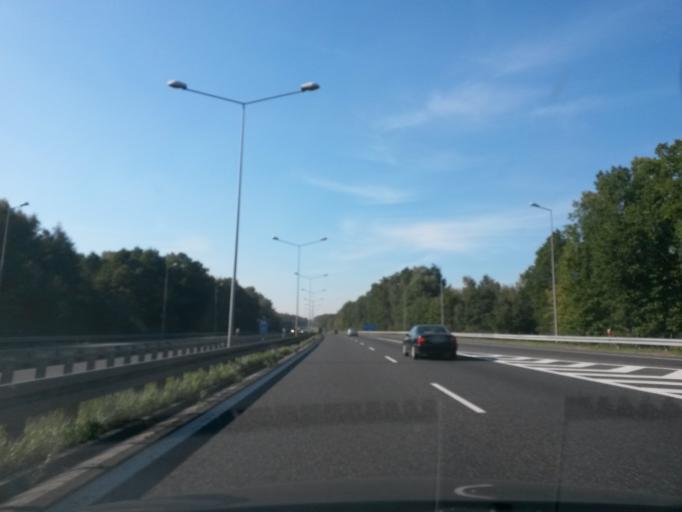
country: PL
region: Opole Voivodeship
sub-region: Powiat strzelecki
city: Ujazd
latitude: 50.4256
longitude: 18.3891
